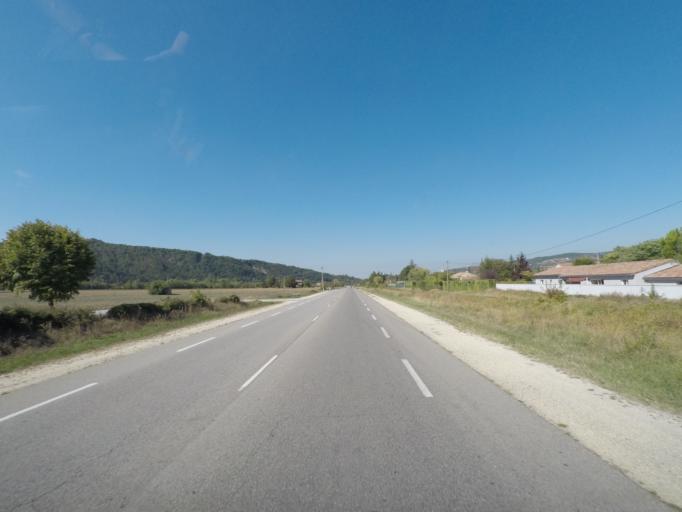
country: FR
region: Rhone-Alpes
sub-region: Departement de la Drome
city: Aouste-sur-Sye
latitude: 44.7121
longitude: 5.0535
